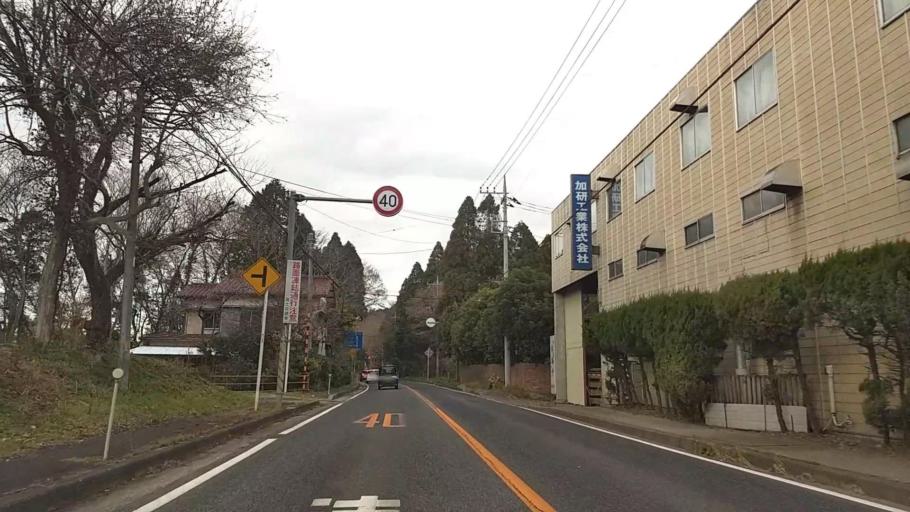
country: JP
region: Chiba
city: Oami
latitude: 35.5800
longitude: 140.2638
